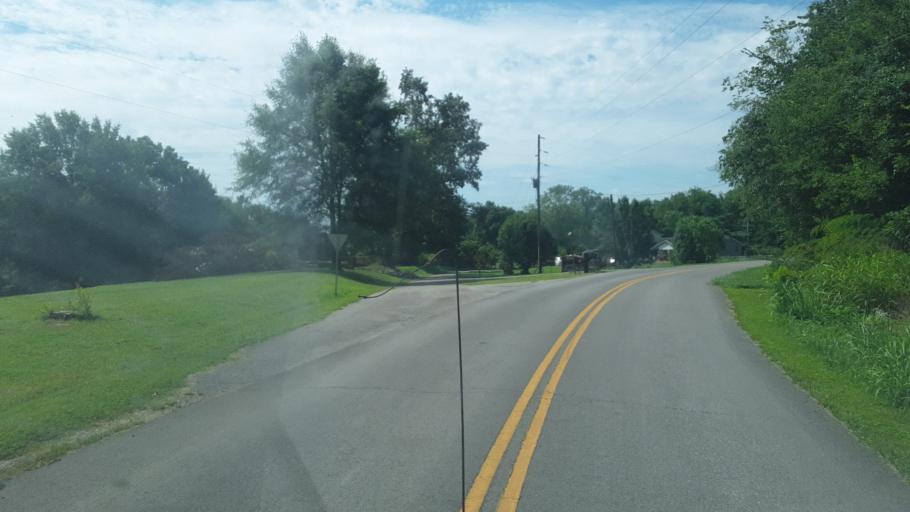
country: US
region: Kentucky
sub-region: Christian County
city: Oak Grove
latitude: 36.7327
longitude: -87.3217
